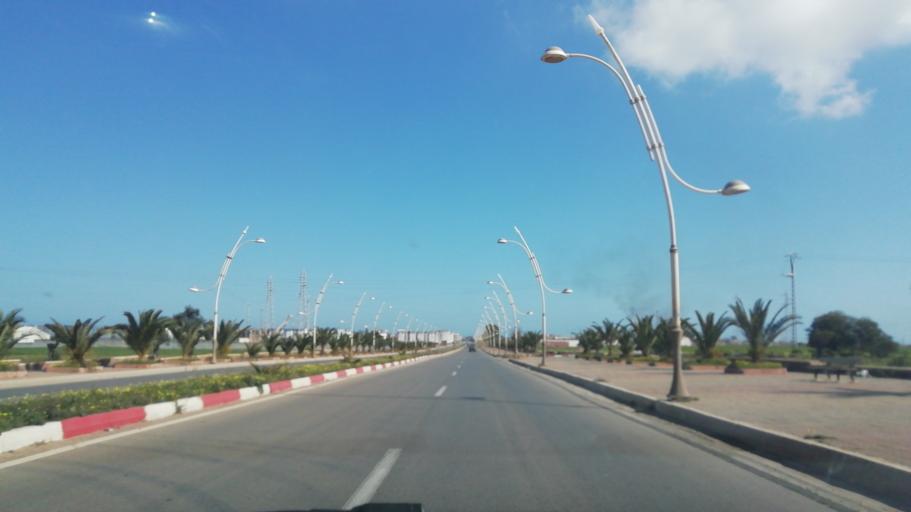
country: DZ
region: Oran
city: Ain el Bya
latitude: 35.7913
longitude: -0.2798
